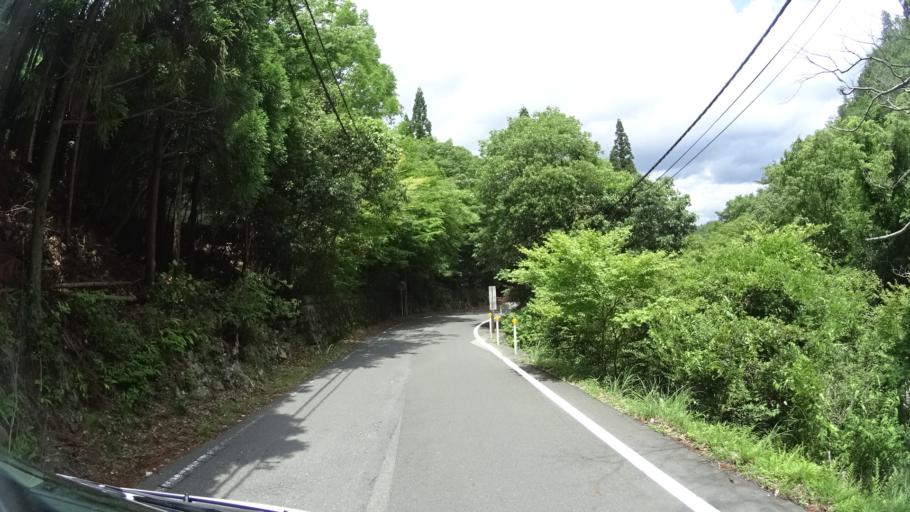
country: JP
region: Kyoto
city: Kameoka
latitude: 35.0452
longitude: 135.4117
